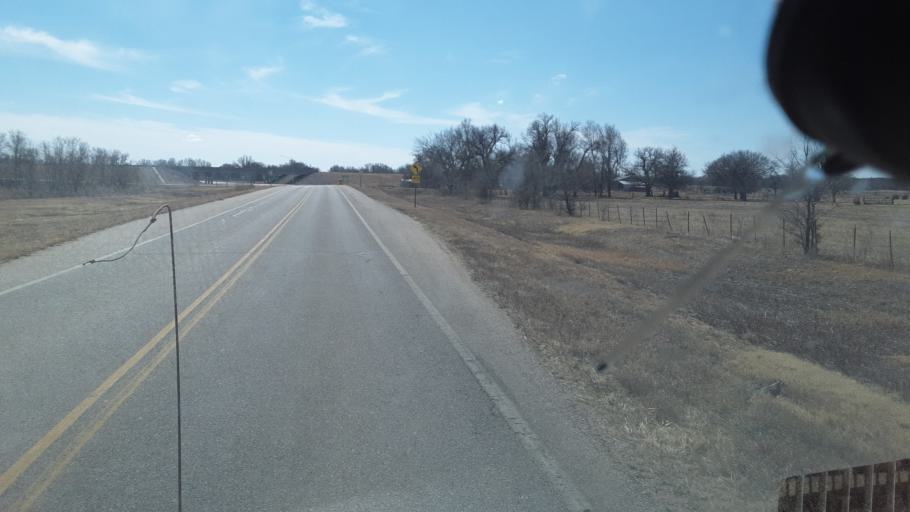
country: US
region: Kansas
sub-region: Reno County
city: Buhler
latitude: 38.1570
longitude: -97.8489
